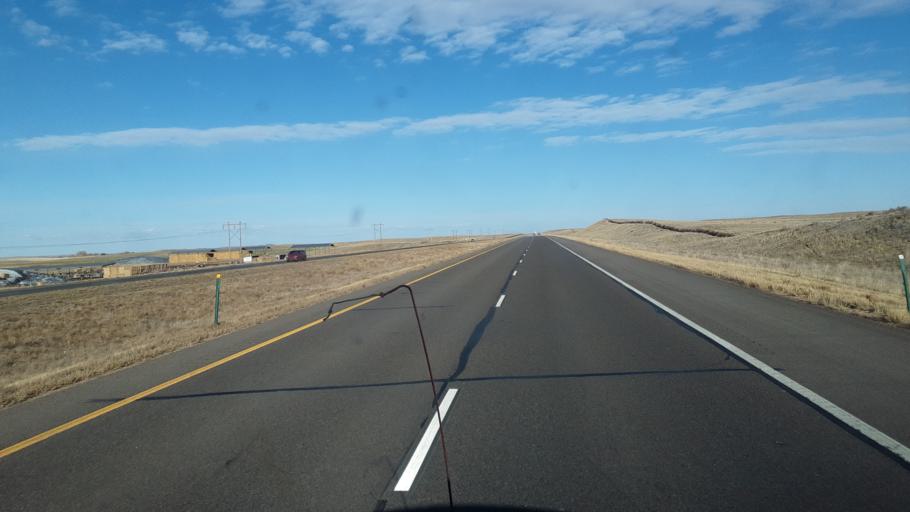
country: US
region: Colorado
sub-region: Morgan County
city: Brush
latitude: 40.3343
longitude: -103.4697
